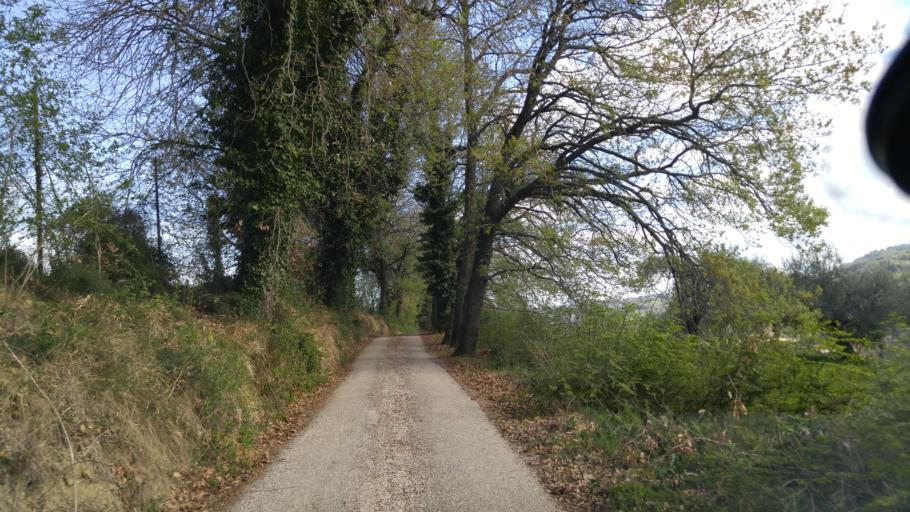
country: IT
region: The Marches
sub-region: Provincia di Pesaro e Urbino
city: Fenile
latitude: 43.8462
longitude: 12.9610
